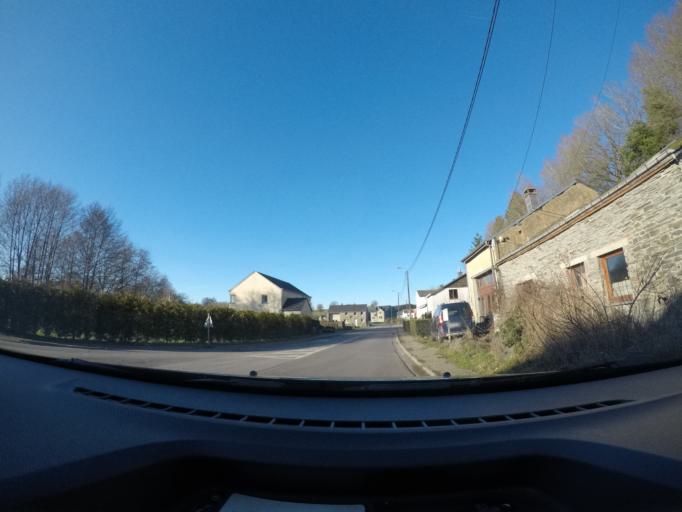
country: BE
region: Wallonia
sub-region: Province du Luxembourg
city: Bertrix
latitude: 49.8366
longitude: 5.2995
